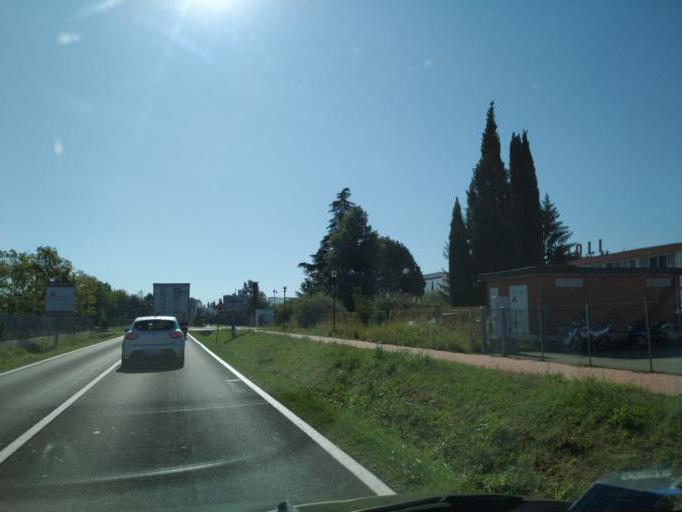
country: IT
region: Emilia-Romagna
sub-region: Provincia di Bologna
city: Sant'Agata Bolognese
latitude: 44.6605
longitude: 11.1233
